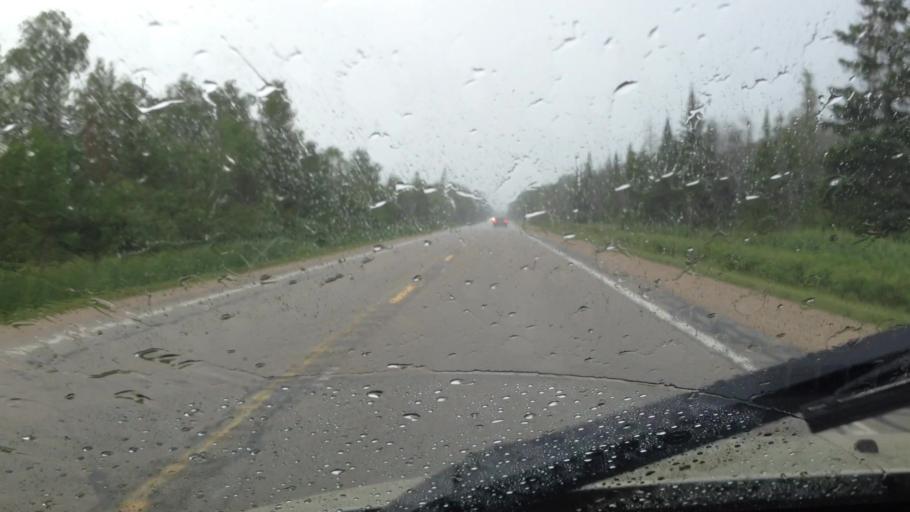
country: US
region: Michigan
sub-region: Menominee County
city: Menominee
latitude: 45.3916
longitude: -87.3698
